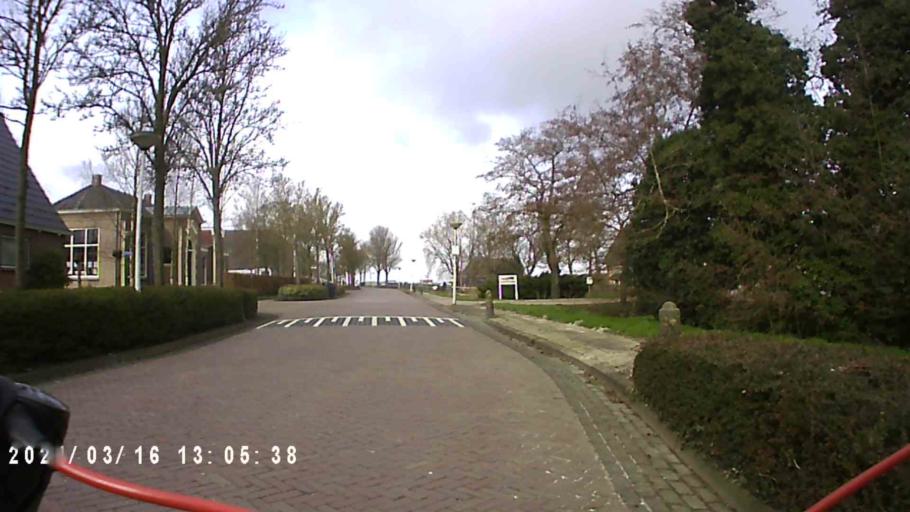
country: NL
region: Friesland
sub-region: Menameradiel
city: Berltsum
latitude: 53.2523
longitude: 5.6265
